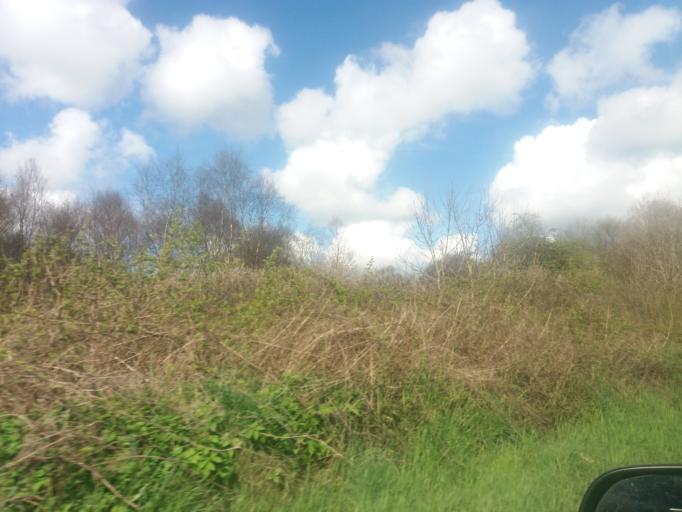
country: IE
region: Ulster
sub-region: An Cabhan
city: Virginia
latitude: 53.8449
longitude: -7.0967
